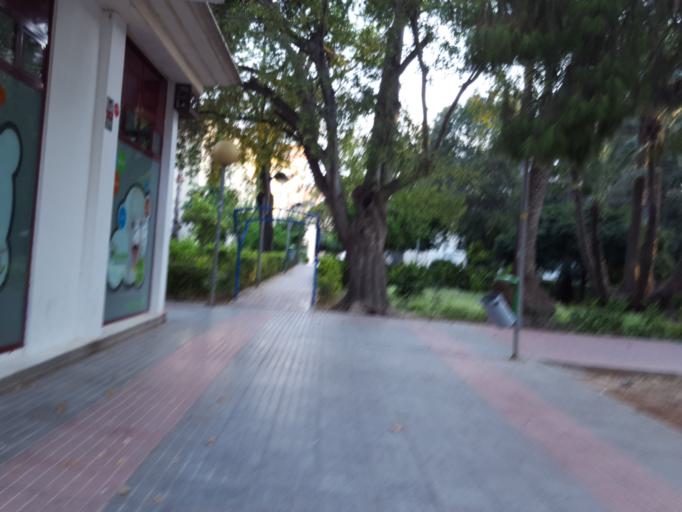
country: ES
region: Murcia
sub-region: Murcia
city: Murcia
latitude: 37.9891
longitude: -1.1377
